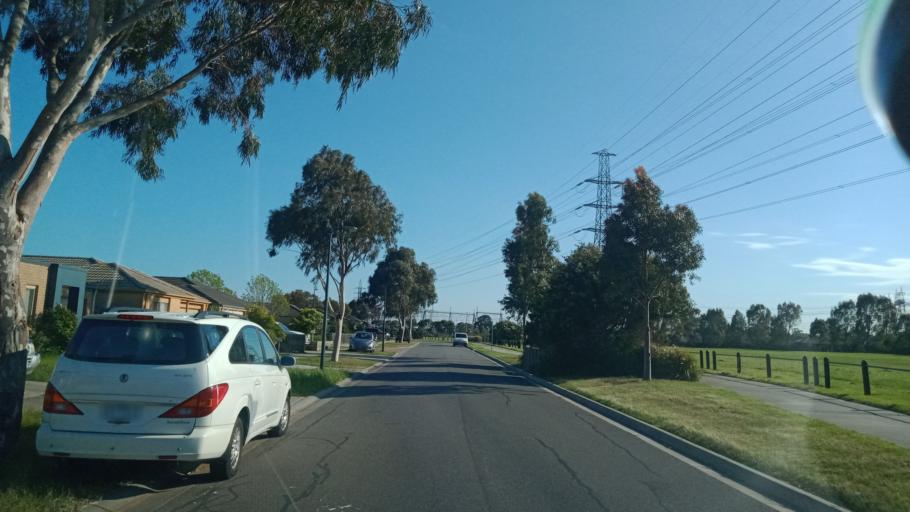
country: AU
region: Victoria
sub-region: Casey
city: Cranbourne West
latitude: -38.0912
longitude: 145.2653
